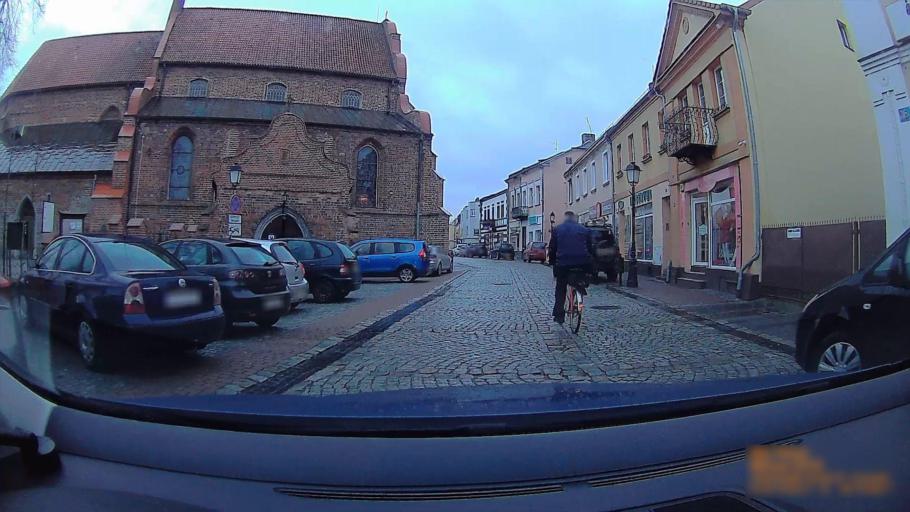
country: PL
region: Greater Poland Voivodeship
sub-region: Konin
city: Konin
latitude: 52.2096
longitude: 18.2546
